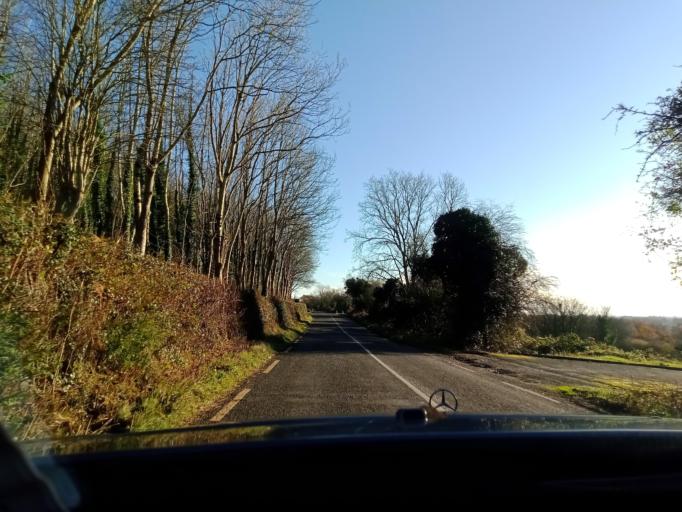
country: IE
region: Leinster
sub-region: Kilkenny
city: Piltown
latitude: 52.3978
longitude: -7.3767
